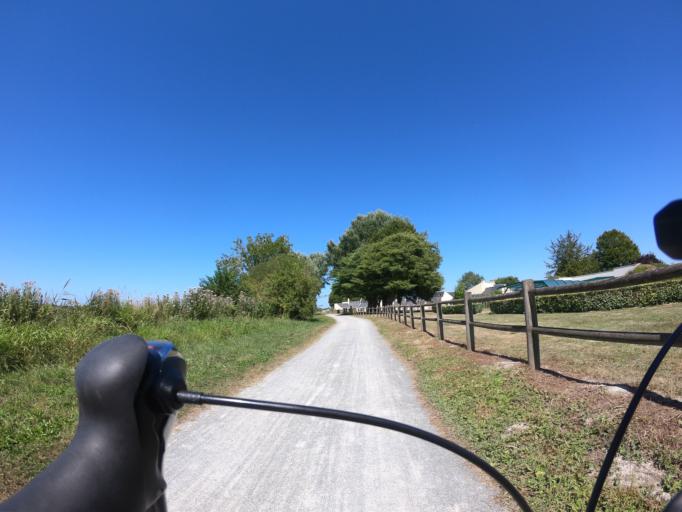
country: FR
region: Lower Normandy
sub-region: Departement de la Manche
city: Pontorson
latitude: 48.5787
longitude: -1.5187
